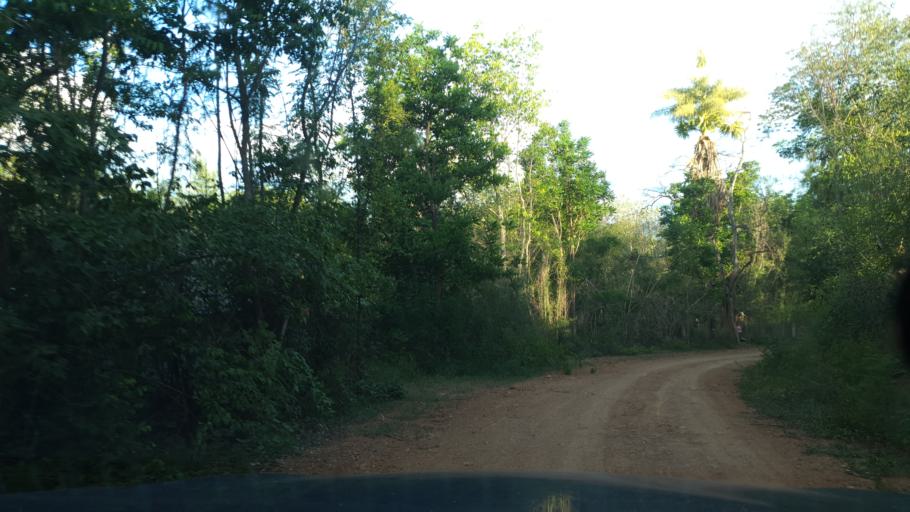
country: TH
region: Lampang
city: Sop Prap
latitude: 17.9547
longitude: 99.3483
